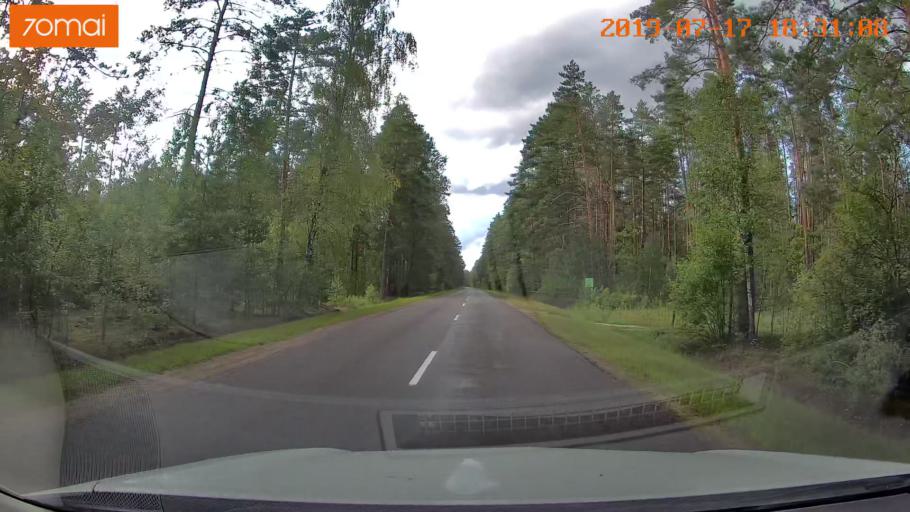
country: BY
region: Mogilev
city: Asipovichy
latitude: 53.2557
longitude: 28.6851
